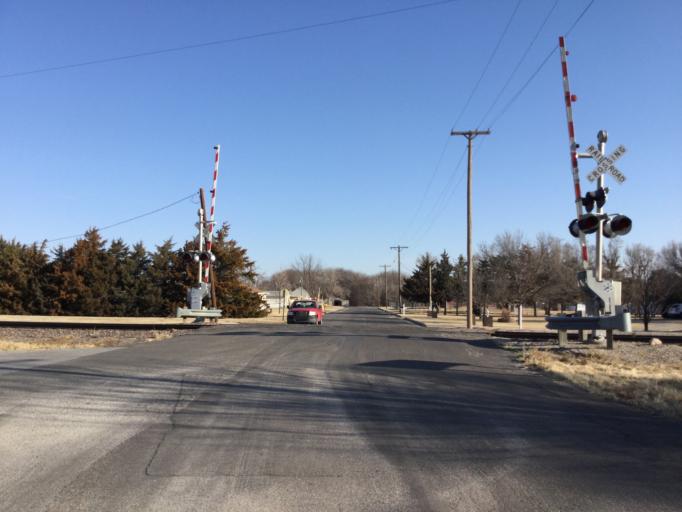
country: US
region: Kansas
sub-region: Rush County
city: La Crosse
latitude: 38.5297
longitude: -99.3012
